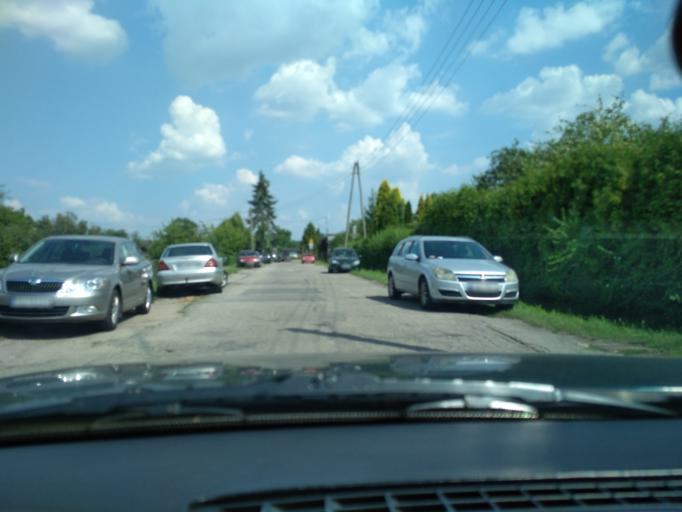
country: PL
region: Silesian Voivodeship
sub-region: Gliwice
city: Gliwice
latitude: 50.2735
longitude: 18.6765
